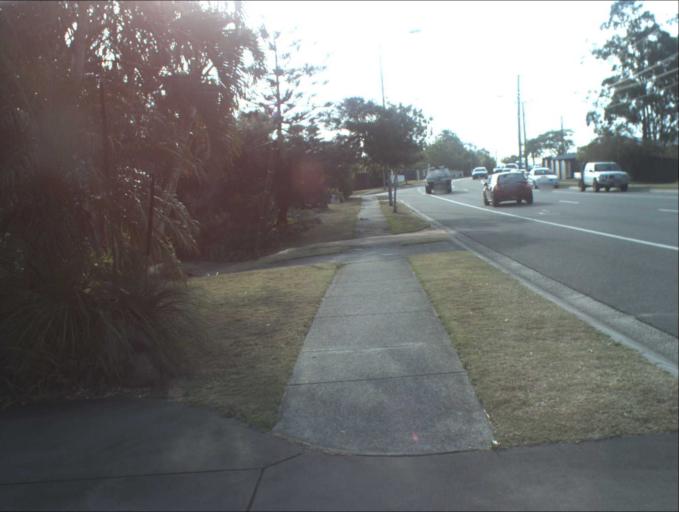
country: AU
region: Queensland
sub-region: Logan
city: Slacks Creek
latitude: -27.6516
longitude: 153.1859
